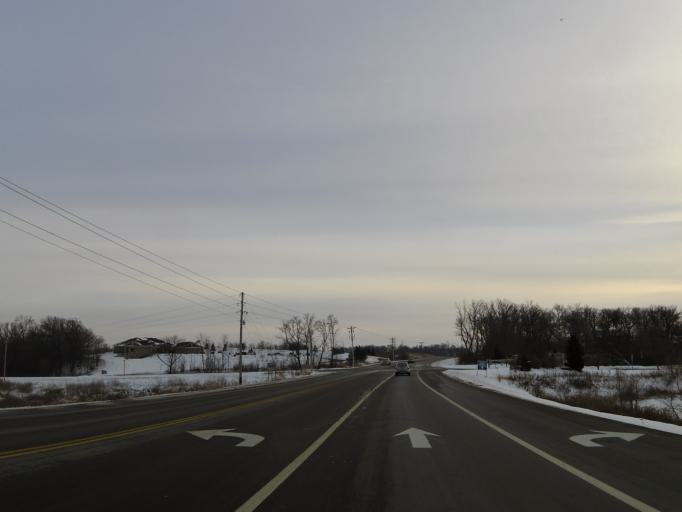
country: US
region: Minnesota
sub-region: Carver County
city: Victoria
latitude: 44.8390
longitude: -93.6525
